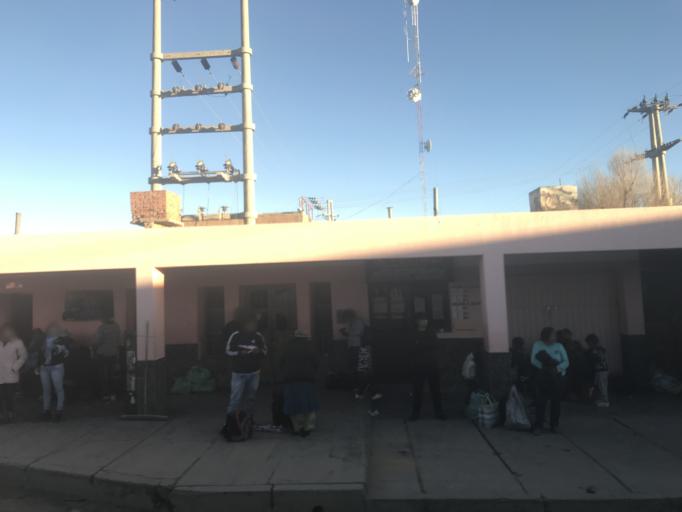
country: AR
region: Jujuy
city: Abra Pampa
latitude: -22.7215
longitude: -65.6972
